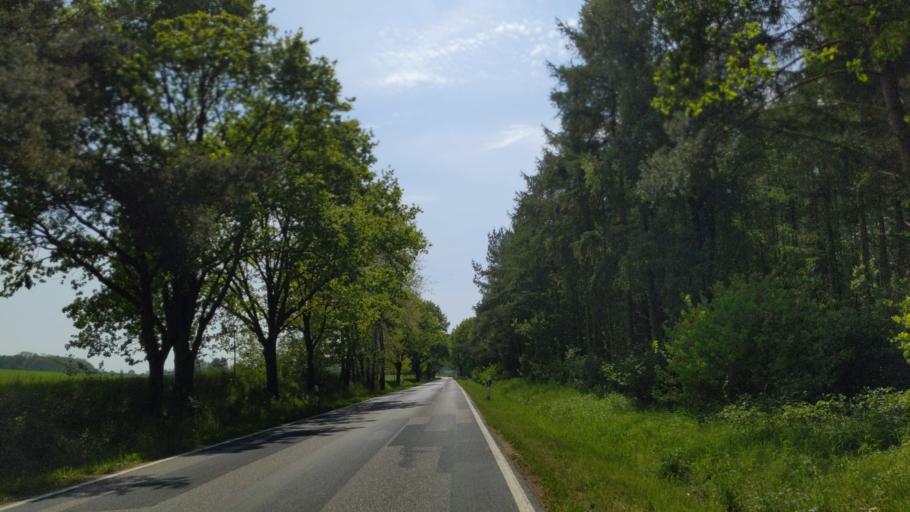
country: DE
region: Mecklenburg-Vorpommern
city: Selmsdorf
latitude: 53.8734
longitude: 10.8363
